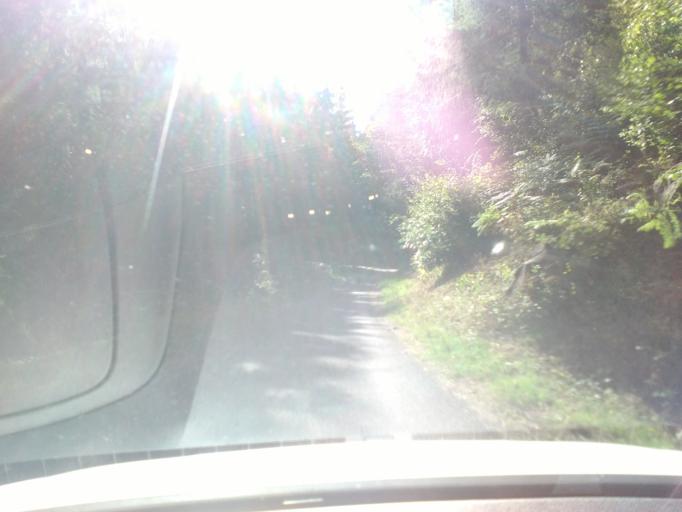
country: FR
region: Lorraine
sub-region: Departement des Vosges
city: Sainte-Marguerite
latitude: 48.3034
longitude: 7.0255
